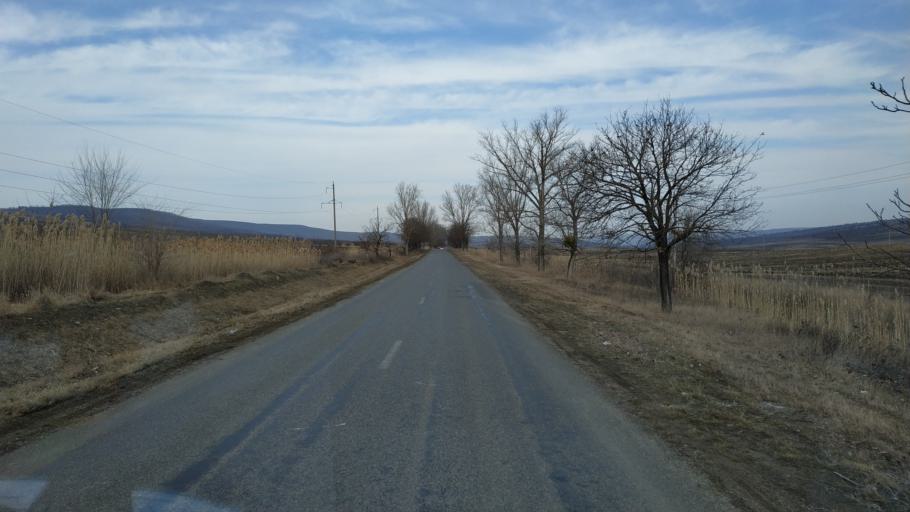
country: MD
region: Nisporeni
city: Nisporeni
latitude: 47.0941
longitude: 28.1344
